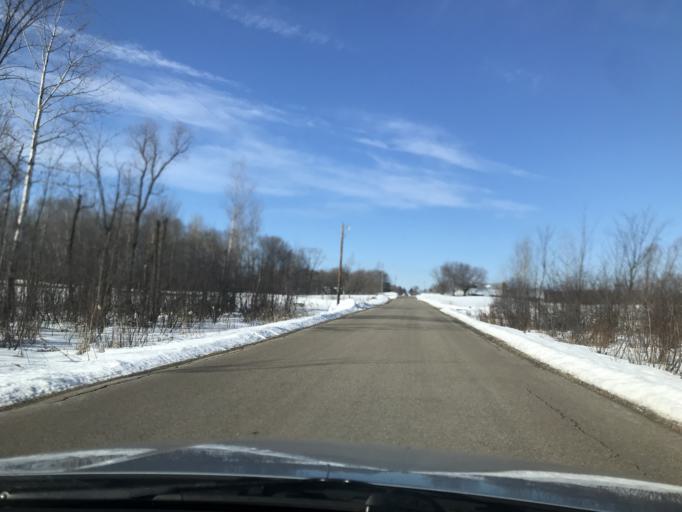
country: US
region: Wisconsin
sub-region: Oconto County
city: Gillett
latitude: 44.9395
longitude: -88.2439
